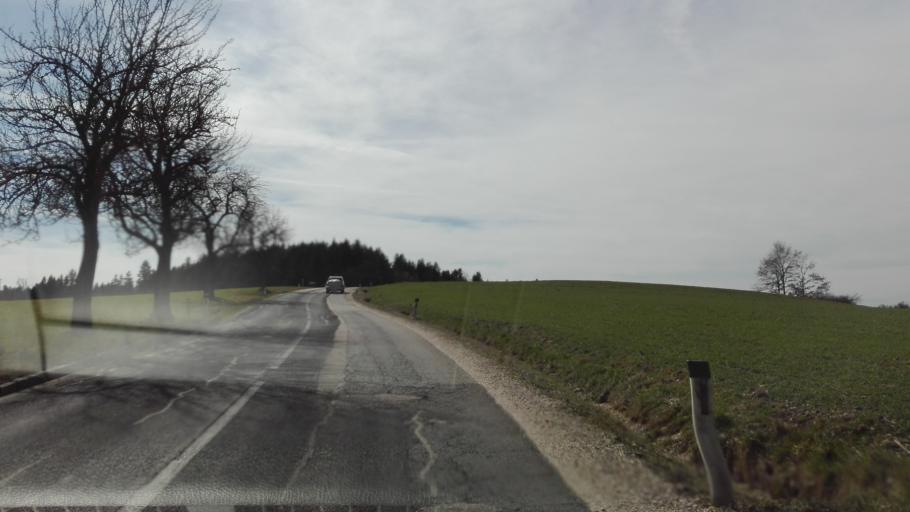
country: AT
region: Upper Austria
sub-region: Politischer Bezirk Scharding
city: Sankt Marienkirchen bei Schaerding
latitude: 48.3719
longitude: 13.6097
